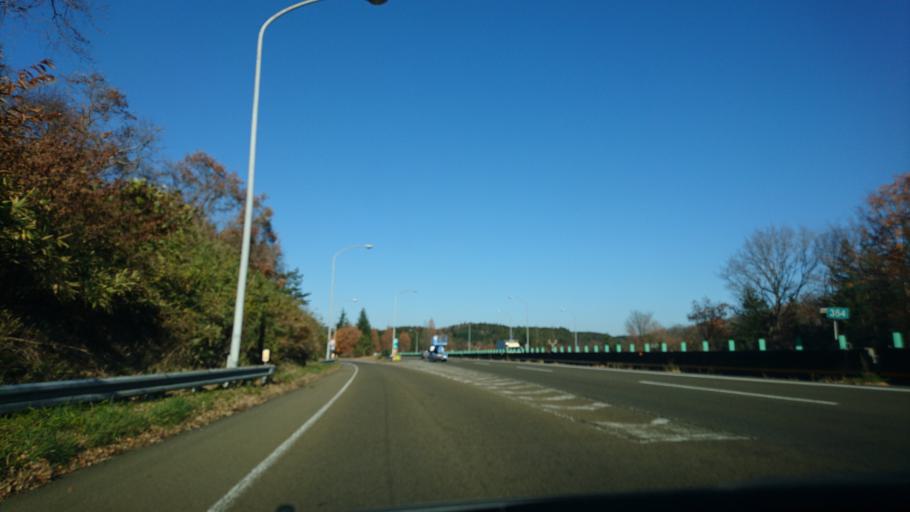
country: JP
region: Miyagi
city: Tomiya
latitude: 38.4100
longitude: 140.9140
